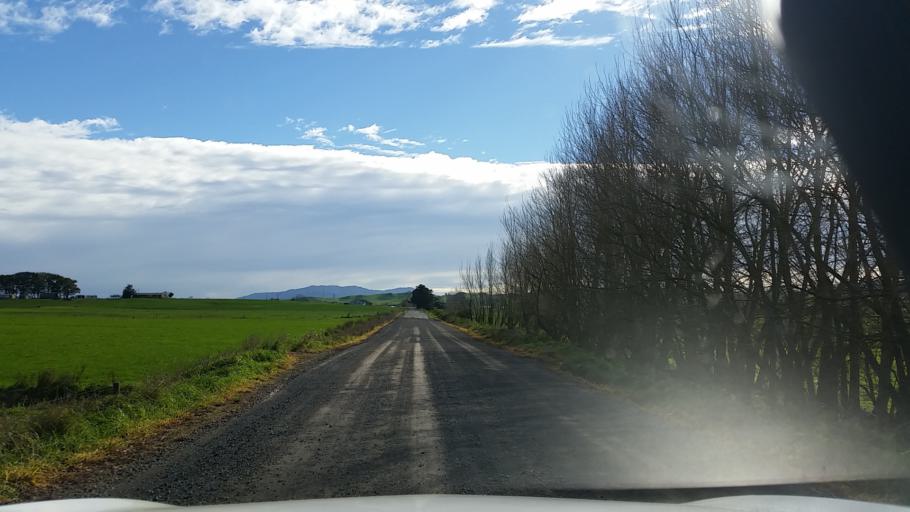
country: NZ
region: Waikato
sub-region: Hamilton City
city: Hamilton
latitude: -37.6273
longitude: 175.4273
